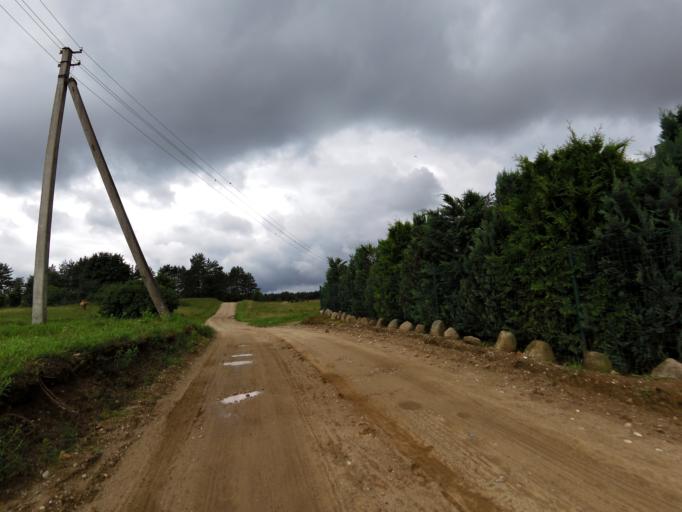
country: LT
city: Grigiskes
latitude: 54.7037
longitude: 25.1067
